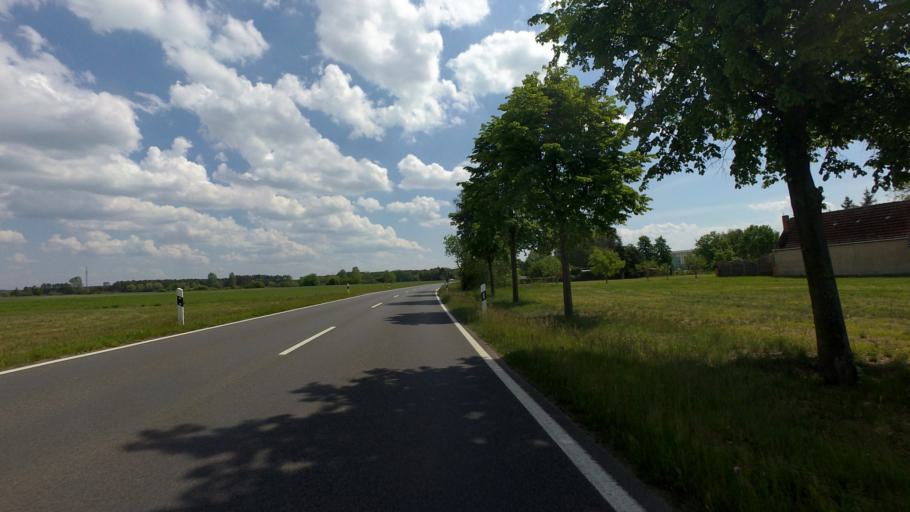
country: DE
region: Brandenburg
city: Lubbenau
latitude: 51.9450
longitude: 13.9830
